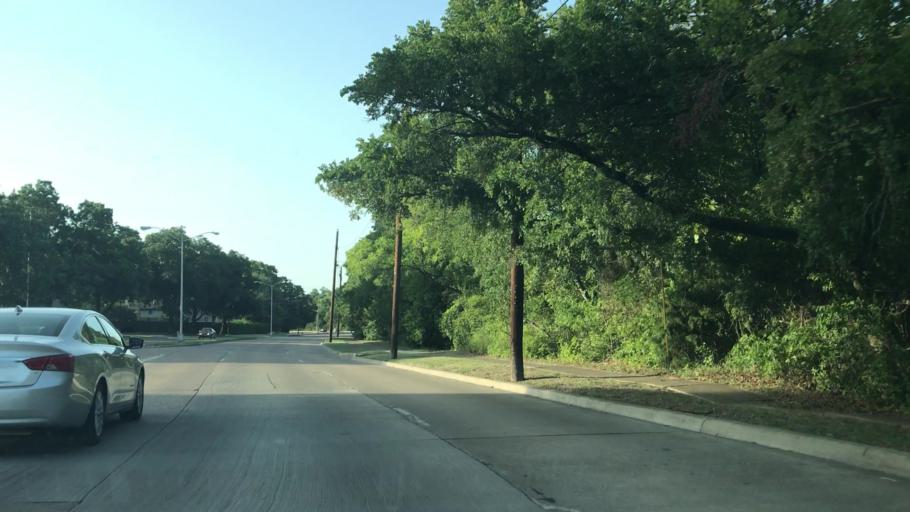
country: US
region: Texas
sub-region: Dallas County
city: Garland
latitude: 32.8557
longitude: -96.7012
